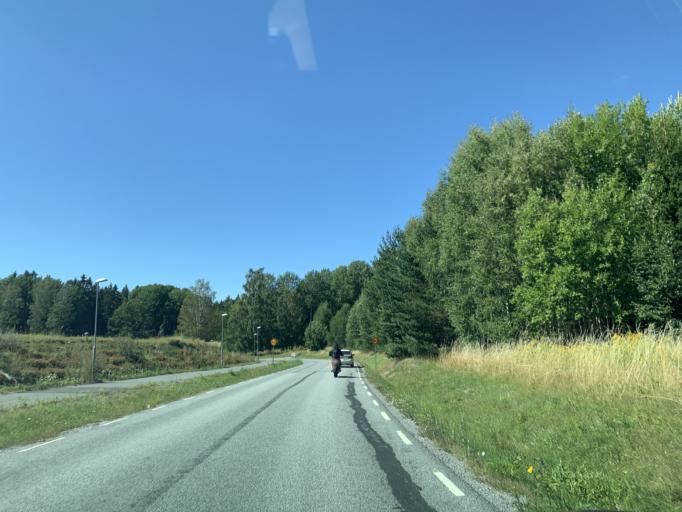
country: SE
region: Stockholm
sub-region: Ekero Kommun
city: Ekeroe
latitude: 59.2723
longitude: 17.8171
